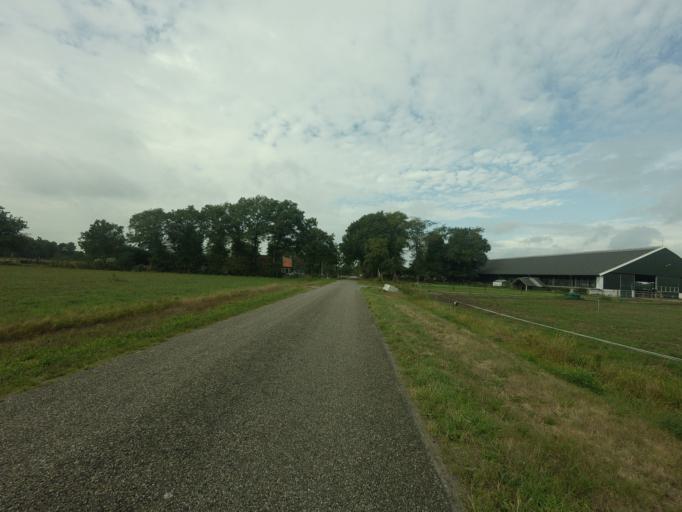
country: NL
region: Friesland
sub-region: Gemeente Heerenveen
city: Jubbega
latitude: 52.9684
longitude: 6.1631
